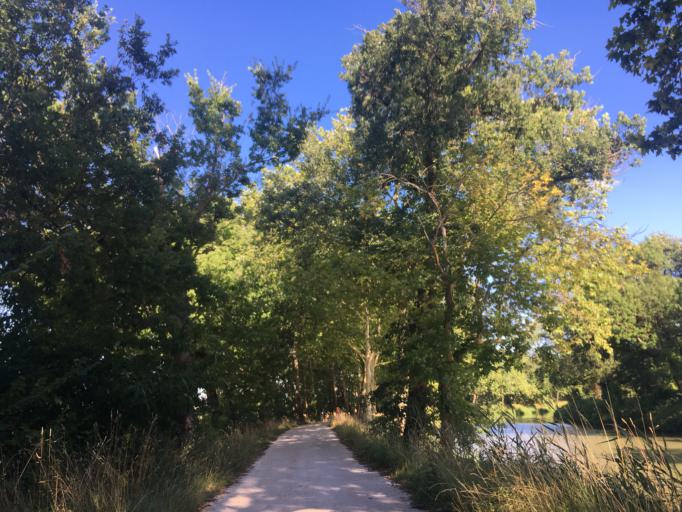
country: FR
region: Midi-Pyrenees
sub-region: Departement de la Haute-Garonne
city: Gardouch
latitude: 43.3977
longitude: 1.6815
